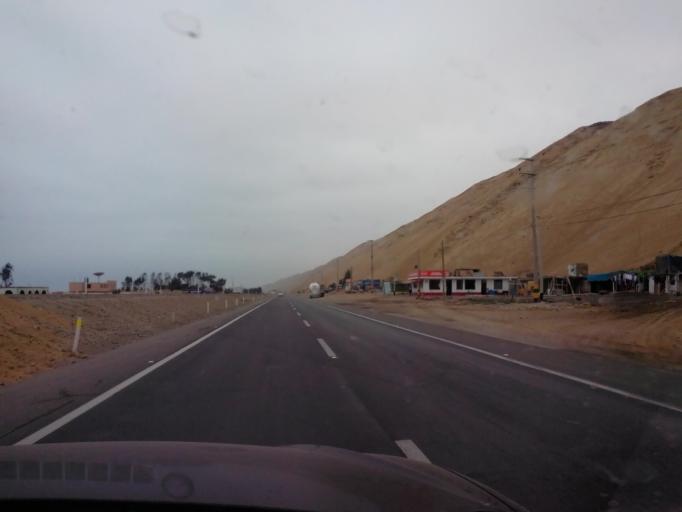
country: PE
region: Ica
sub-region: Provincia de Chincha
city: San Pedro
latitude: -13.3699
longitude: -76.2112
